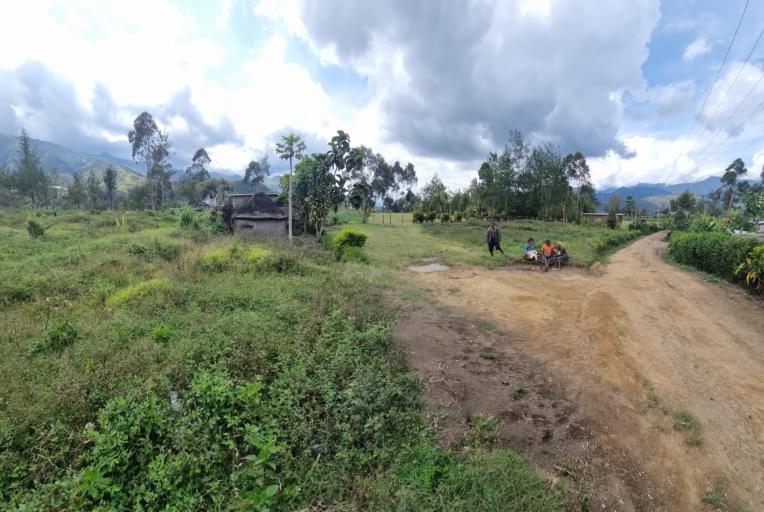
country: PG
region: Enga
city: Wabag
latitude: -5.6150
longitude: 143.8479
